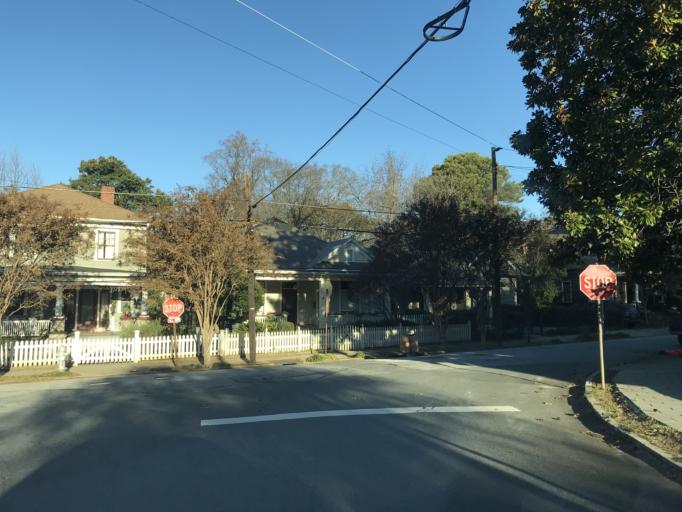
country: US
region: Georgia
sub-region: DeKalb County
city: Druid Hills
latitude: 33.7643
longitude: -84.3535
